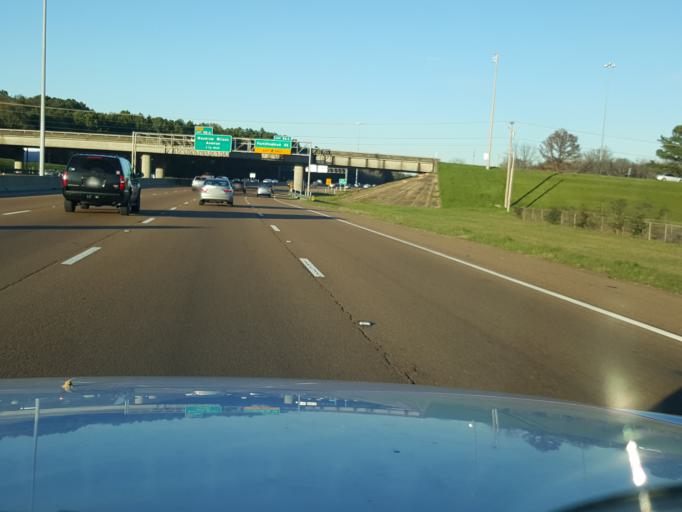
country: US
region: Mississippi
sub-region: Hinds County
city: Jackson
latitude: 32.3085
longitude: -90.1639
